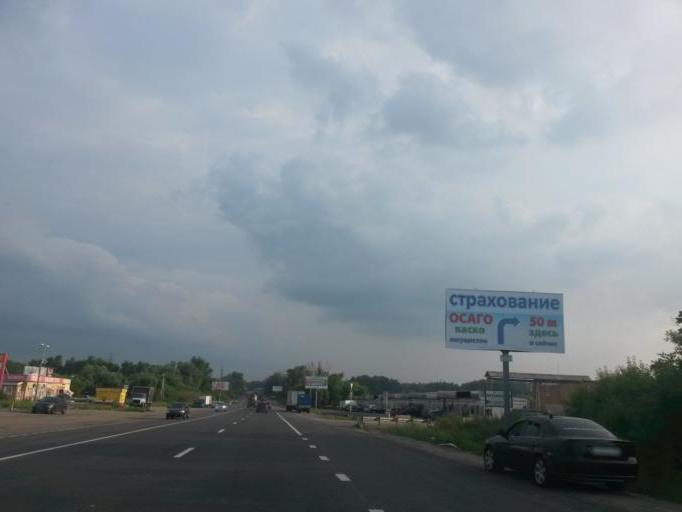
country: RU
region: Moskovskaya
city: Petrovskaya
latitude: 55.5435
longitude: 37.7728
